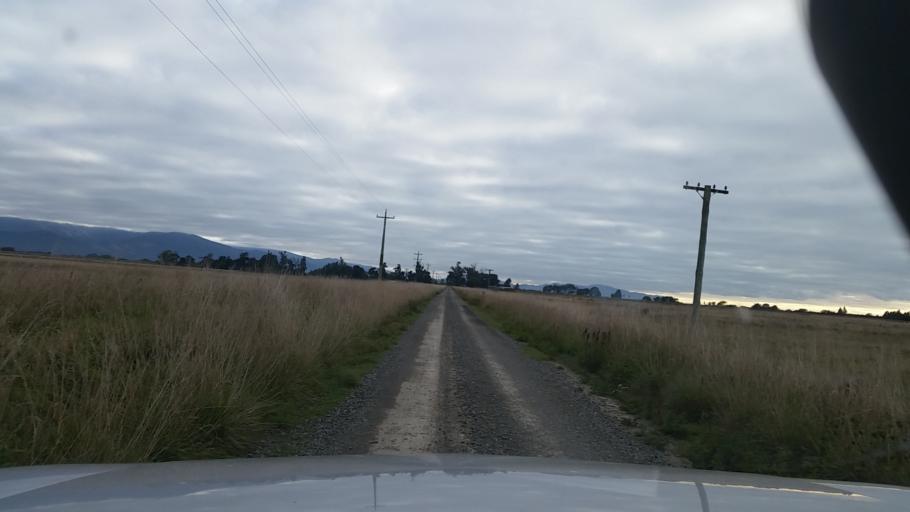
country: NZ
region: Marlborough
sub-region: Marlborough District
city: Blenheim
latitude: -41.5067
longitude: 174.0304
